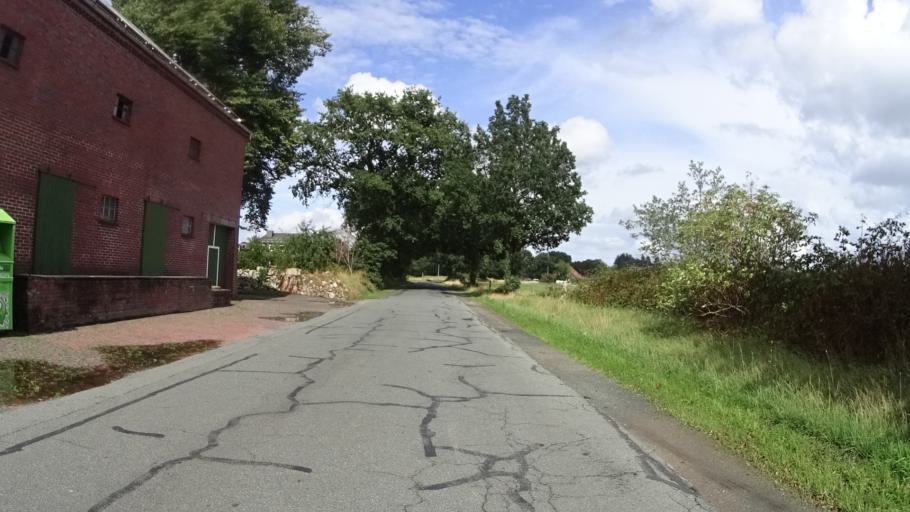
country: DE
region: Lower Saxony
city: Zetel
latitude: 53.3913
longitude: 7.9246
